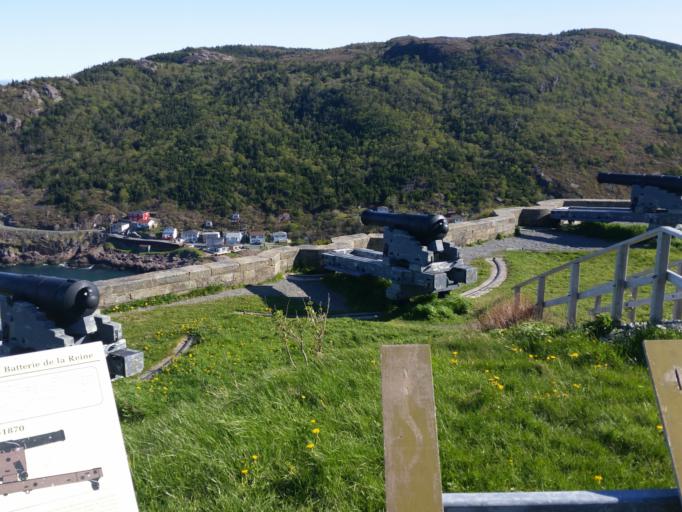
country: CA
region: Newfoundland and Labrador
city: St. John's
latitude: 47.5686
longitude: -52.6857
